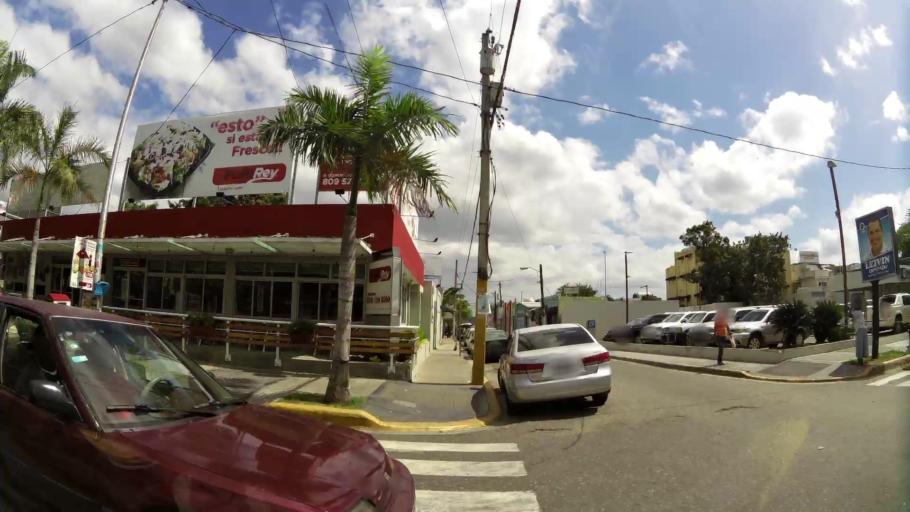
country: DO
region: San Cristobal
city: San Cristobal
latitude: 18.4177
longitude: -70.1117
